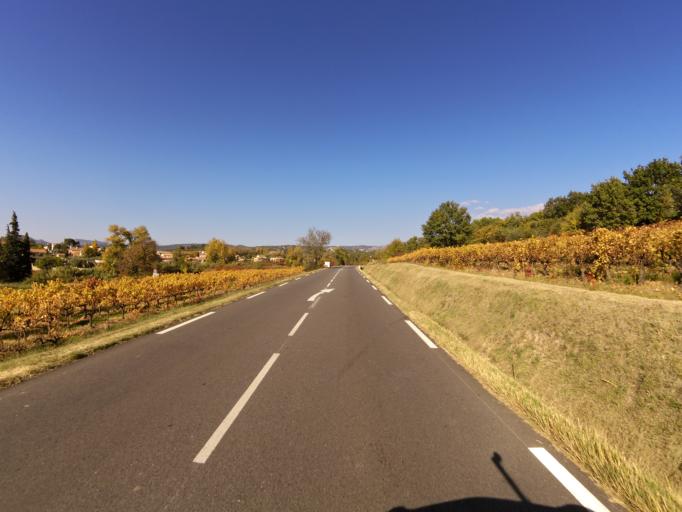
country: FR
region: Provence-Alpes-Cote d'Azur
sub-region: Departement du Vaucluse
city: Caromb
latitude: 44.0977
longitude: 5.1423
